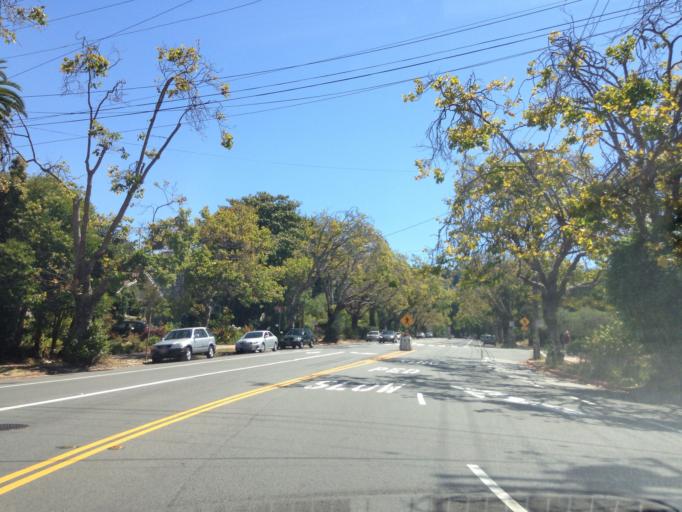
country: US
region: California
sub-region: Alameda County
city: Berkeley
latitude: 37.8891
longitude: -122.2754
